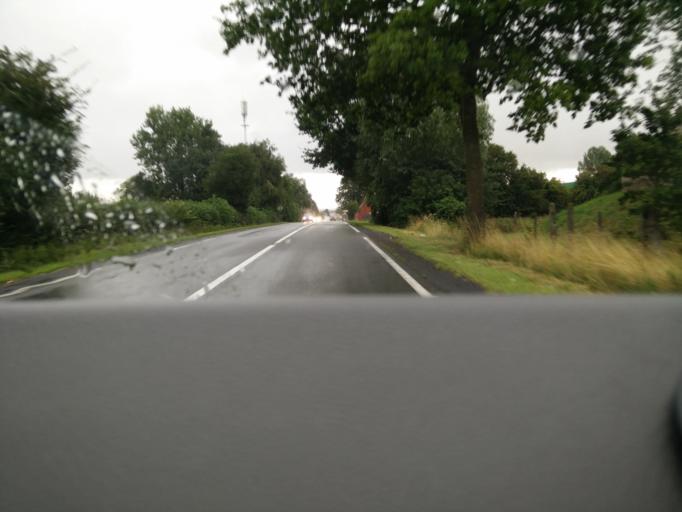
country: FR
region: Nord-Pas-de-Calais
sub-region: Departement du Pas-de-Calais
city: Savy-Berlette
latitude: 50.3563
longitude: 2.4770
